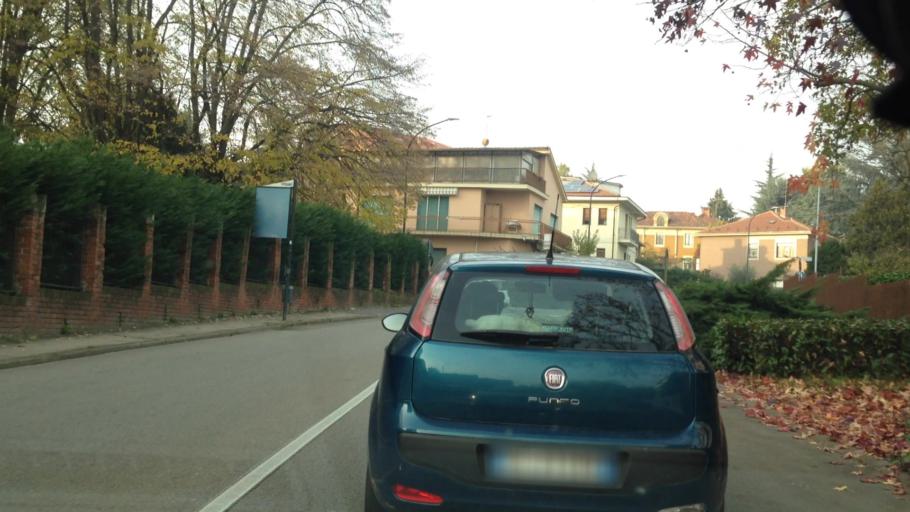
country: IT
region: Piedmont
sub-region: Provincia di Asti
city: Asti
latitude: 44.9068
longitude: 8.2071
